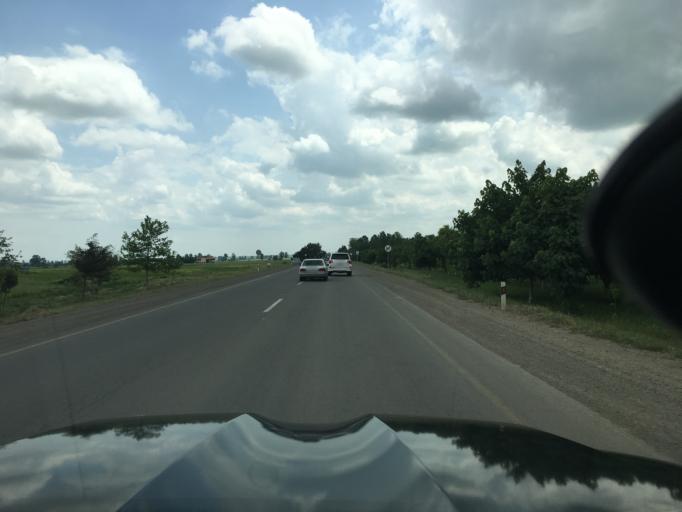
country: AZ
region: Tovuz
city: Tovuz
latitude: 40.9617
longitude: 45.7175
